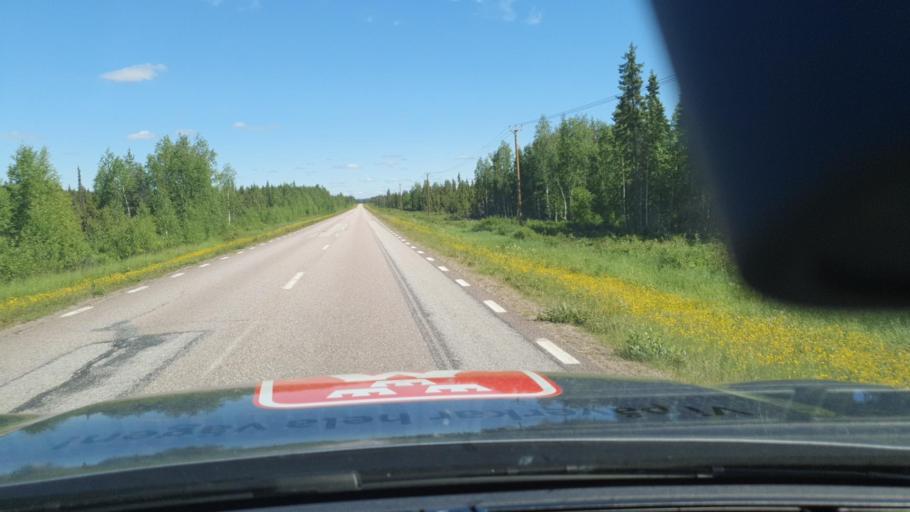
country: SE
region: Norrbotten
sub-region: Overkalix Kommun
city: OEverkalix
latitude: 66.8701
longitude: 22.7580
